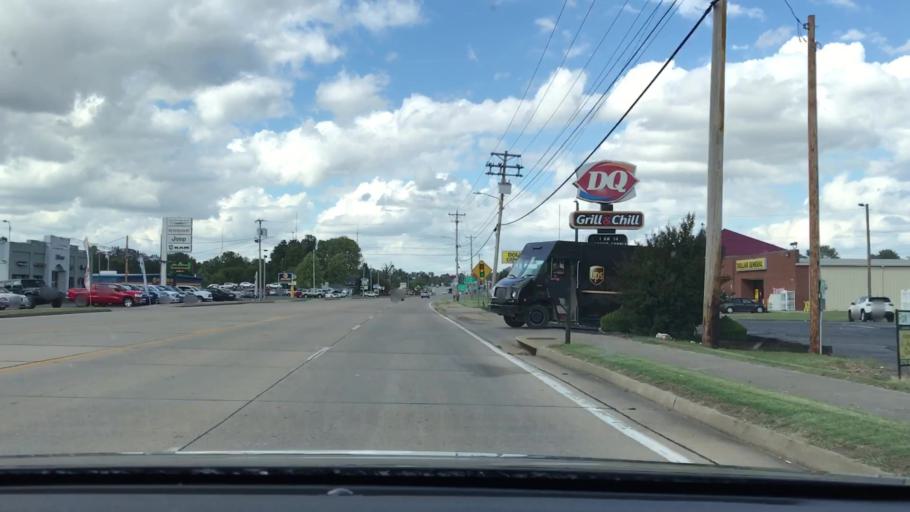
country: US
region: Kentucky
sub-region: Graves County
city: Mayfield
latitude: 36.7530
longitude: -88.6392
